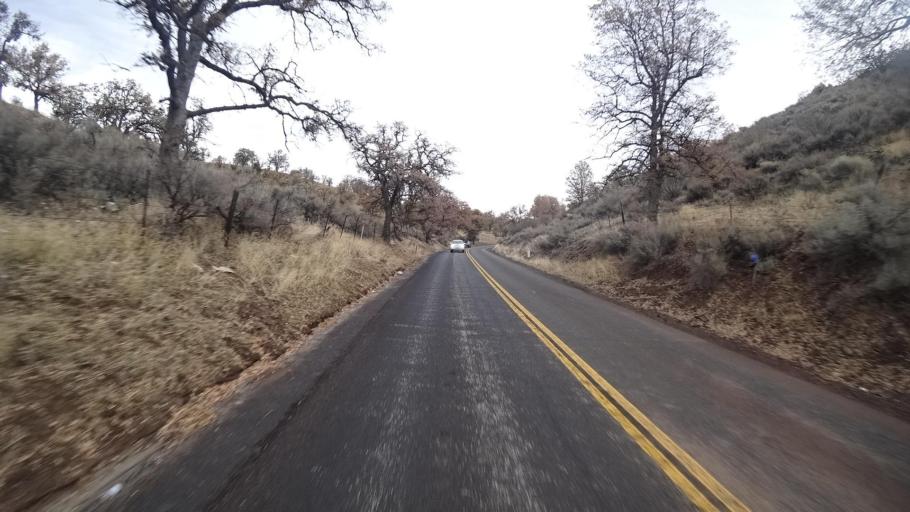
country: US
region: California
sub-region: Kern County
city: Golden Hills
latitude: 35.0963
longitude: -118.5412
